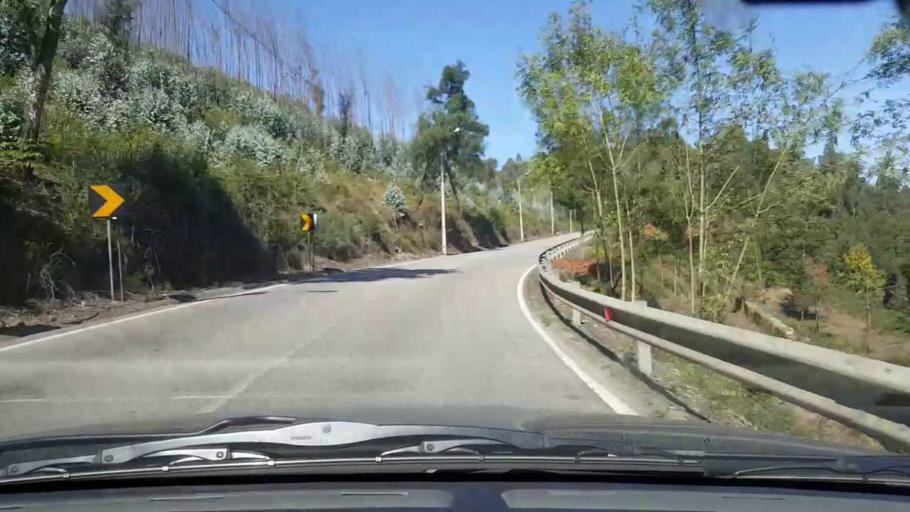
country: PT
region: Braga
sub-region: Vila Nova de Famalicao
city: Ribeirao
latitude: 41.3369
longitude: -8.6231
